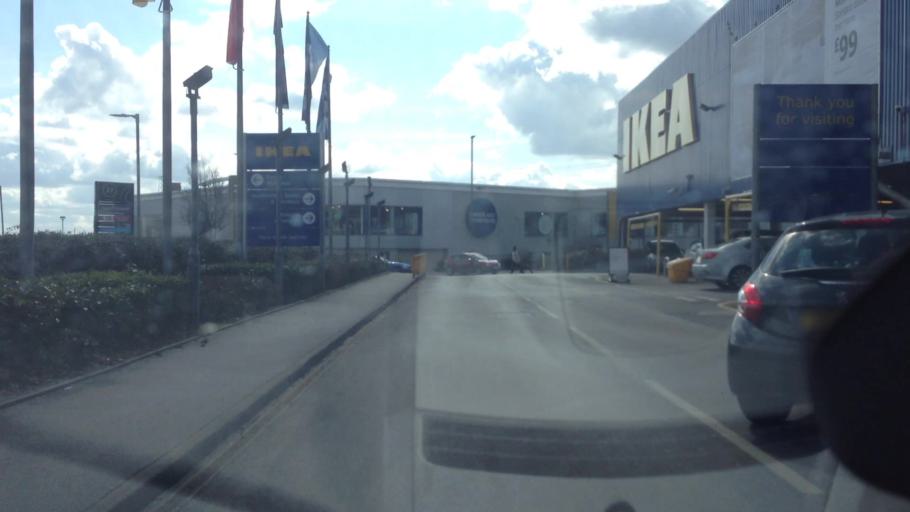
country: GB
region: England
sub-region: City and Borough of Leeds
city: Drighlington
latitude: 53.7453
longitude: -1.6466
